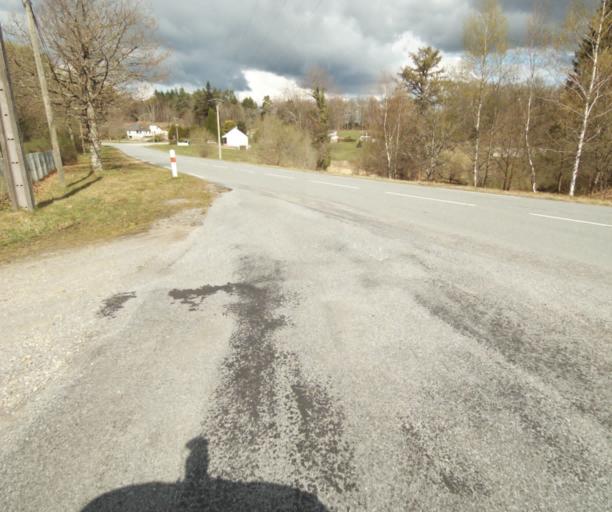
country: FR
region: Limousin
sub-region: Departement de la Correze
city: Correze
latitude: 45.2891
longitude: 1.8997
